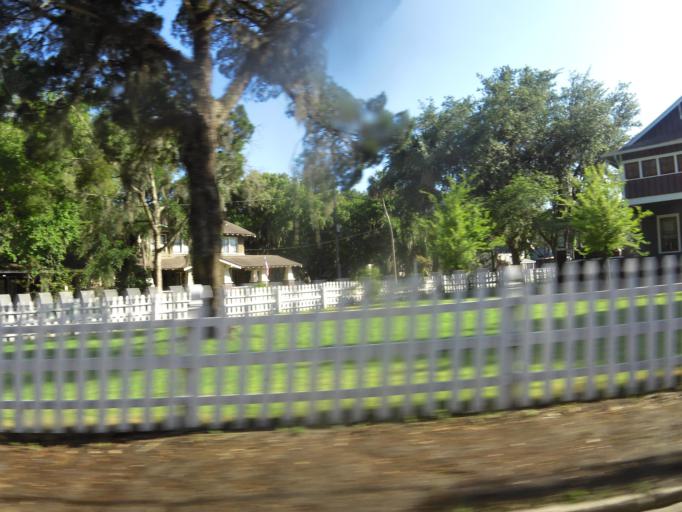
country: US
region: Florida
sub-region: Putnam County
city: Palatka
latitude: 29.6452
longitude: -81.6348
